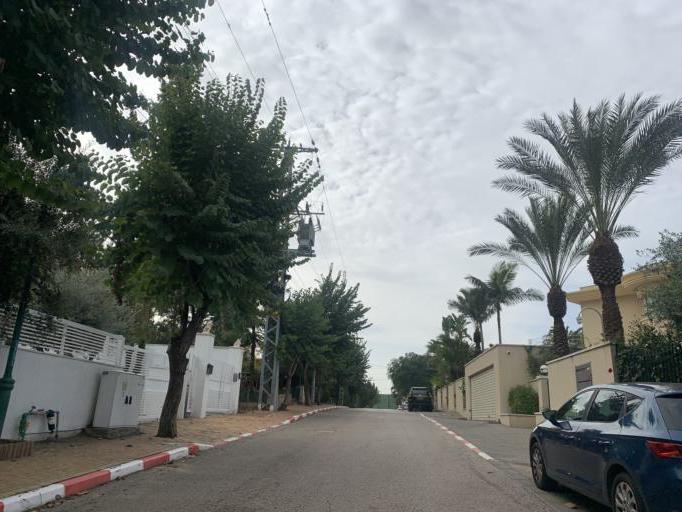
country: IL
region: Central District
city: Hod HaSharon
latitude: 32.1658
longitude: 34.8824
